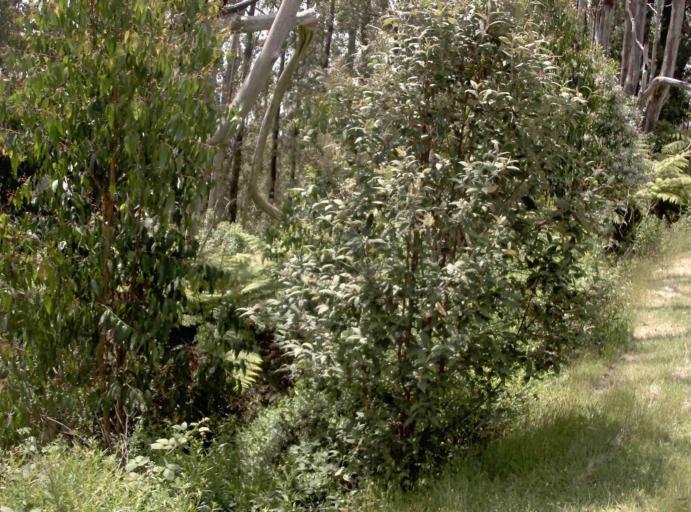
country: AU
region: Victoria
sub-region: Latrobe
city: Traralgon
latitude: -38.4300
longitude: 146.5322
